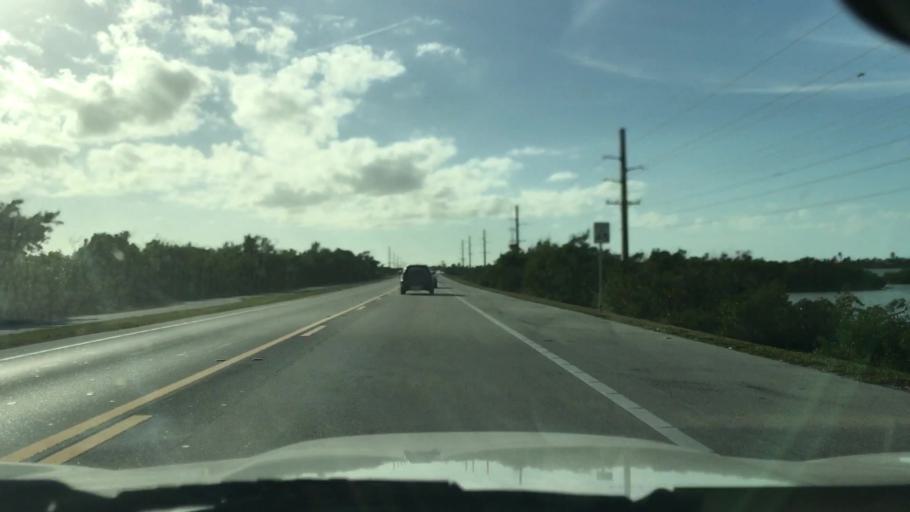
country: US
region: Florida
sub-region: Monroe County
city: Big Pine Key
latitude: 24.6639
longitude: -81.3990
